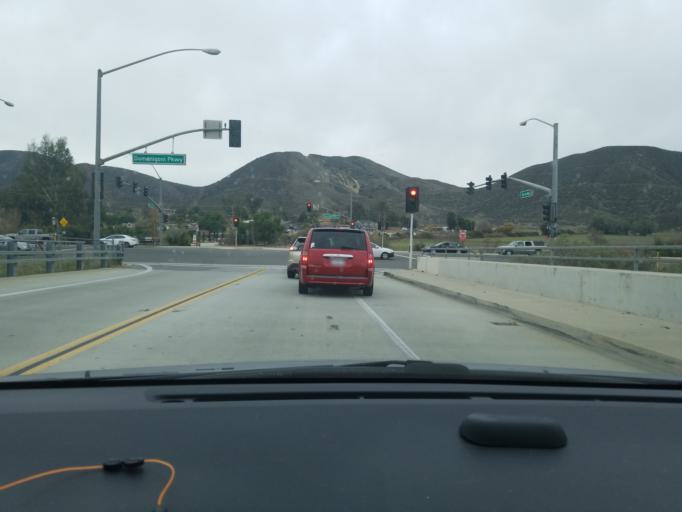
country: US
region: California
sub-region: Riverside County
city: Winchester
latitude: 33.7046
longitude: -117.0343
